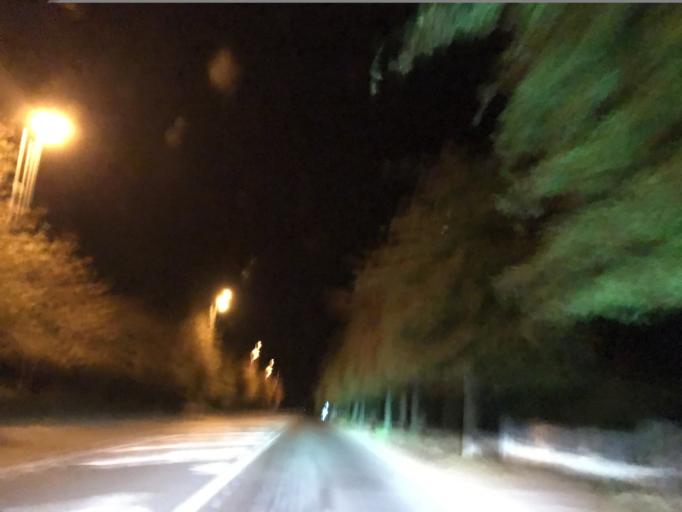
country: FR
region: Auvergne
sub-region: Departement de l'Allier
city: Saint-Yorre
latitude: 46.0533
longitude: 3.4692
